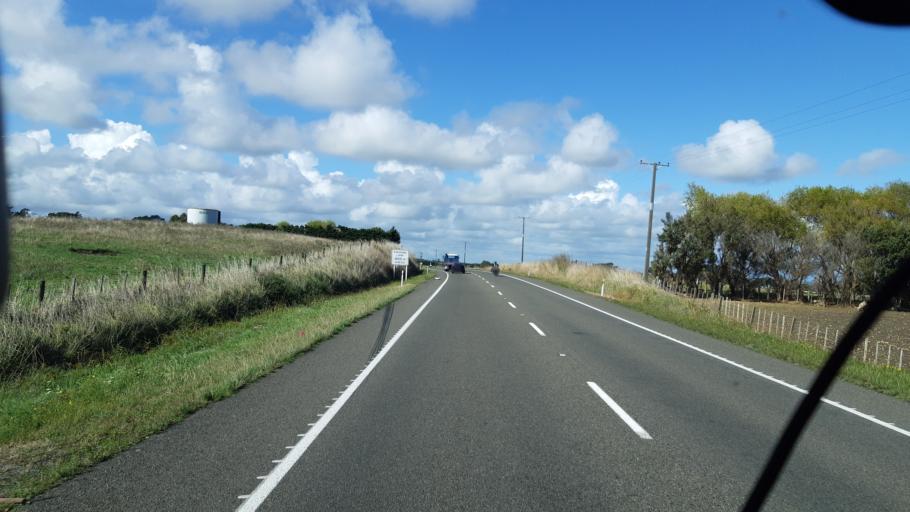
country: NZ
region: Manawatu-Wanganui
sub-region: Wanganui District
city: Wanganui
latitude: -39.9778
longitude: 175.1351
